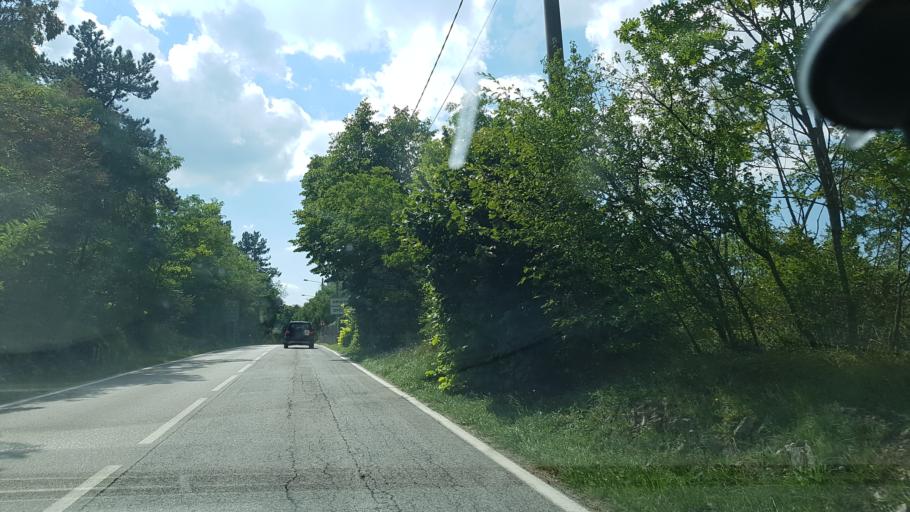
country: IT
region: Friuli Venezia Giulia
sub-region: Provincia di Trieste
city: Villa Opicina
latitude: 45.6953
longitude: 13.7970
